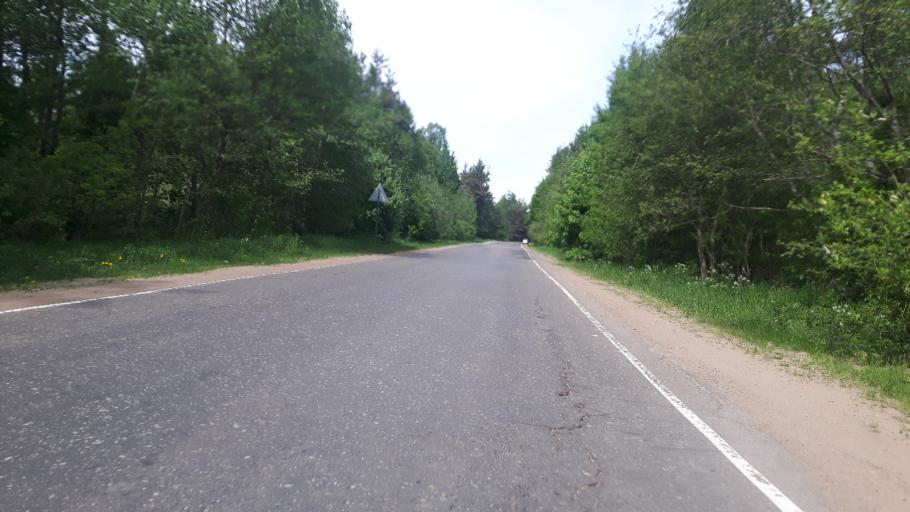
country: RU
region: Leningrad
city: Ust'-Luga
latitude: 59.6471
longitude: 28.2656
